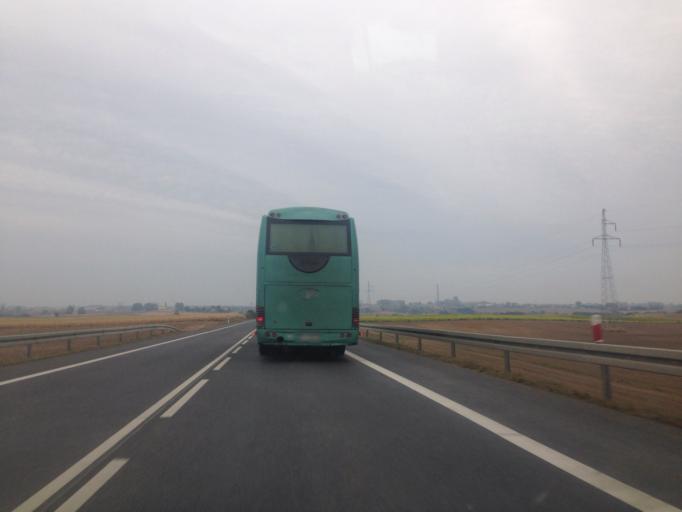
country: PL
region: Greater Poland Voivodeship
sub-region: Powiat gnieznienski
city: Gniezno
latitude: 52.5535
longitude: 17.6558
